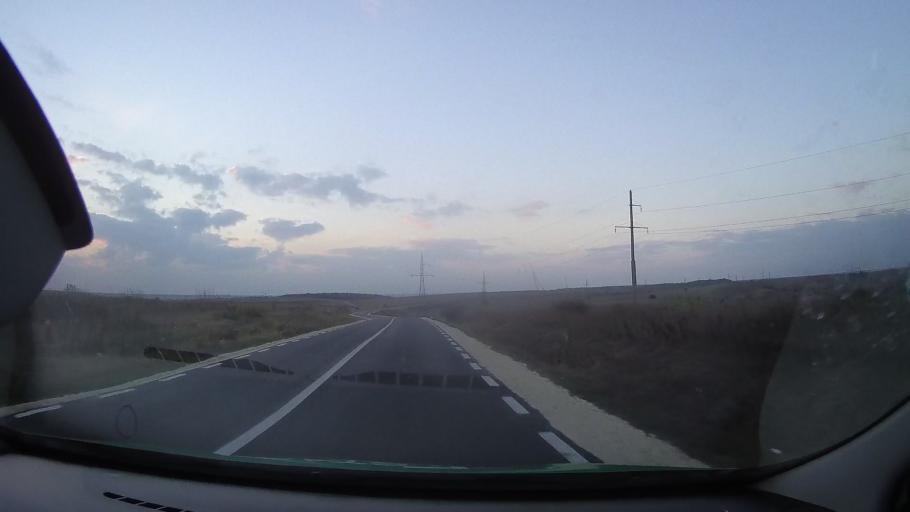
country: RO
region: Constanta
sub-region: Comuna Baneasa
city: Baneasa
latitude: 44.0791
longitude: 27.6934
